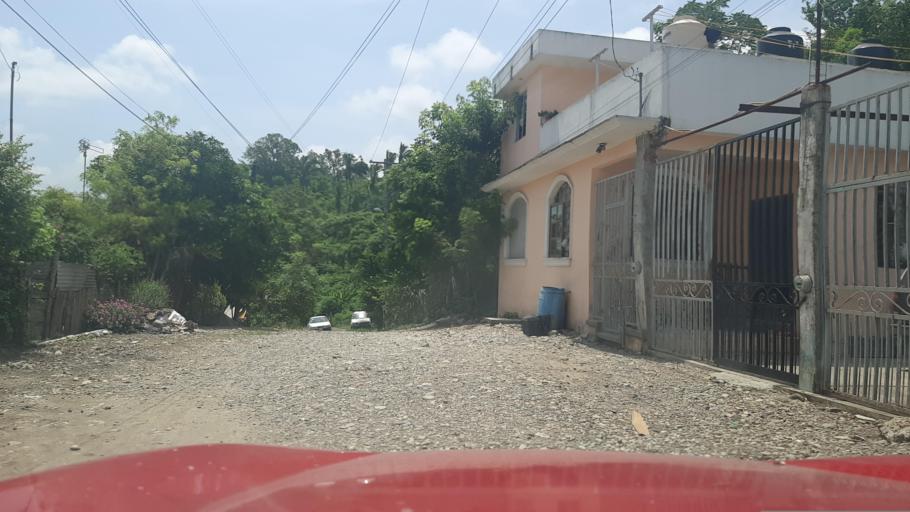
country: MX
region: Veracruz
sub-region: Poza Rica de Hidalgo
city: Arroyo del Maiz Uno
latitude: 20.4979
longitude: -97.4208
